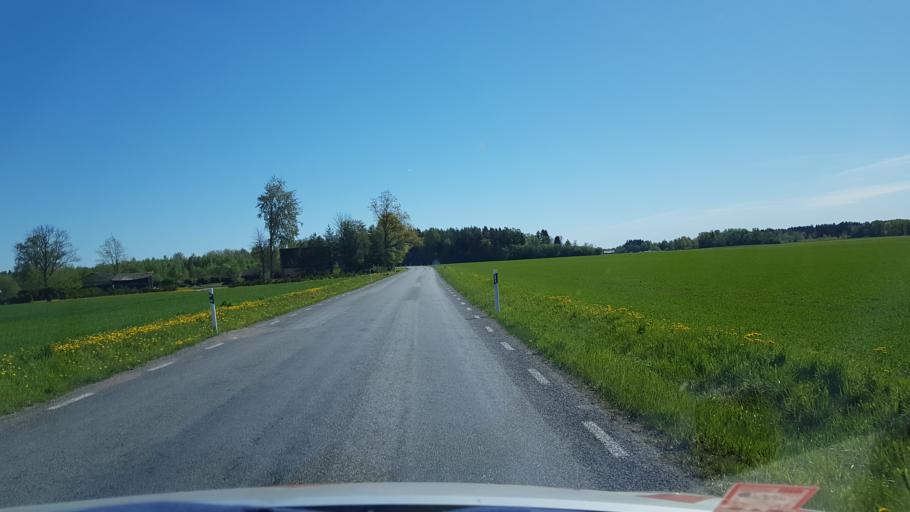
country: EE
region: Tartu
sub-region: Tartu linn
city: Tartu
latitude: 58.4005
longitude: 26.8733
